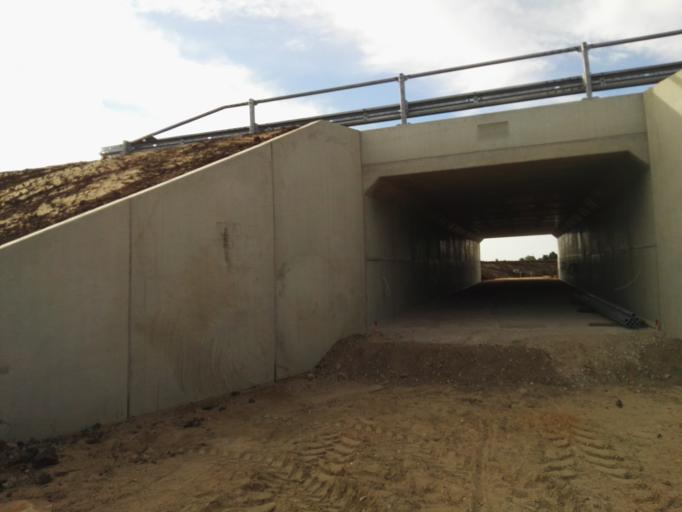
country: DK
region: Capital Region
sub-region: Frederikssund Kommune
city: Frederikssund
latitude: 55.8126
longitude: 12.0886
